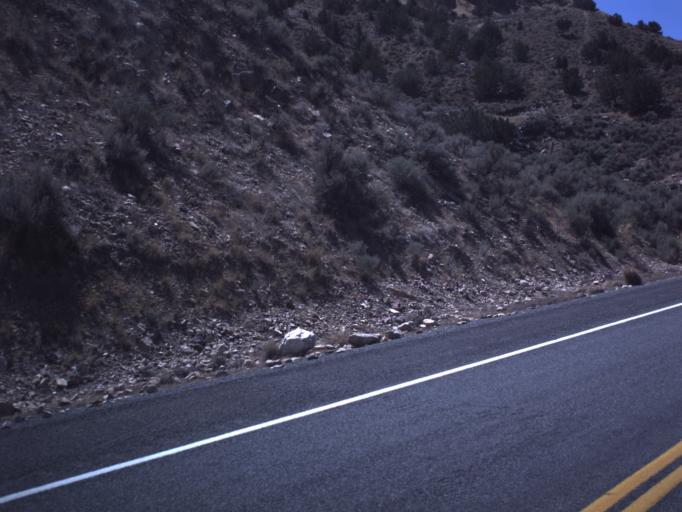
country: US
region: Utah
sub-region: Juab County
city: Nephi
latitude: 39.5572
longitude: -112.2100
